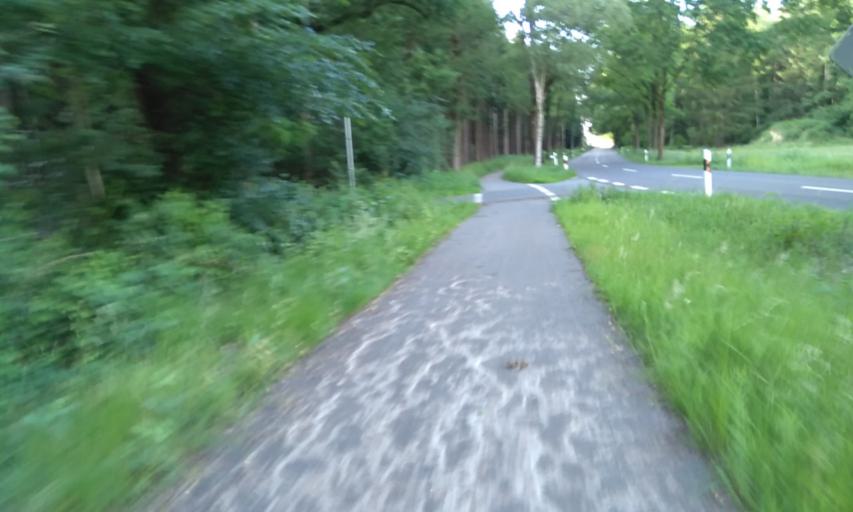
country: DE
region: Lower Saxony
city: Anderlingen
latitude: 53.3621
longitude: 9.3038
